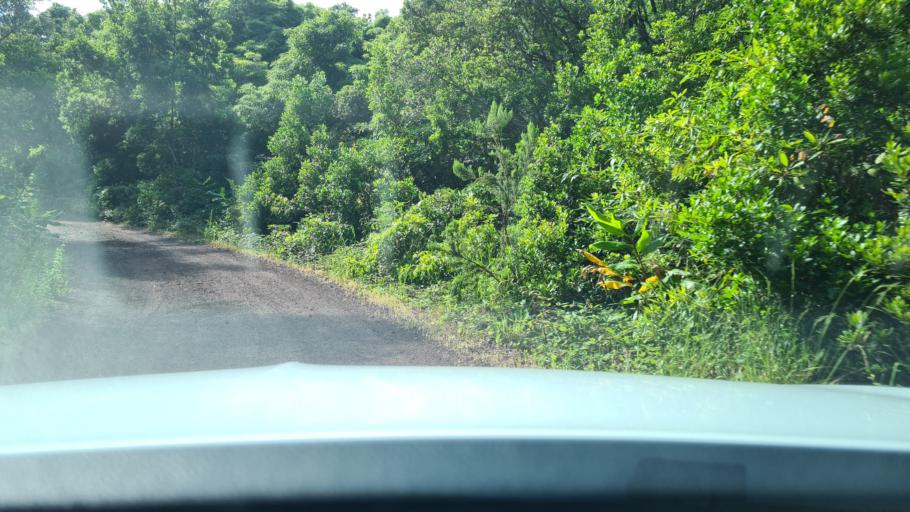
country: PT
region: Azores
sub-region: Sao Roque do Pico
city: Sao Roque do Pico
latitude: 38.4124
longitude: -28.3077
